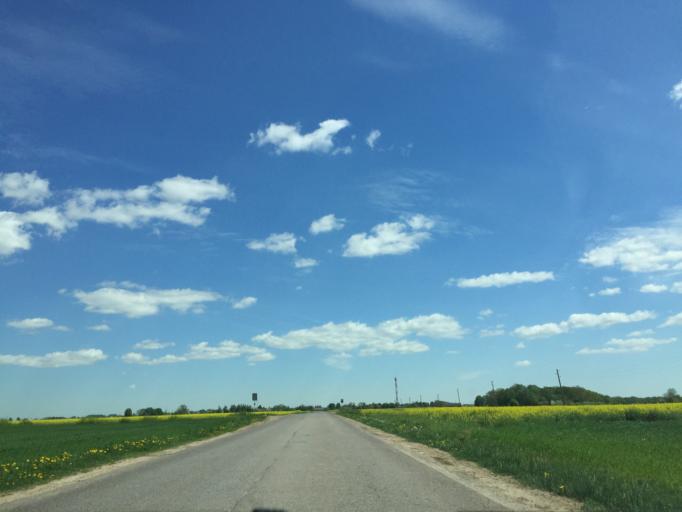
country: LV
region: Bauskas Rajons
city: Bauska
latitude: 56.4092
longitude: 24.1336
